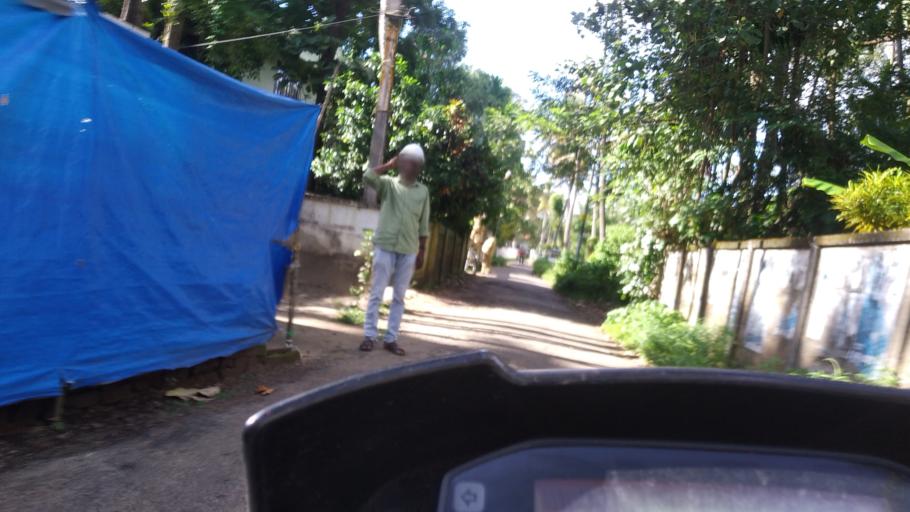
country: IN
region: Kerala
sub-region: Ernakulam
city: Elur
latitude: 10.0710
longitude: 76.2134
